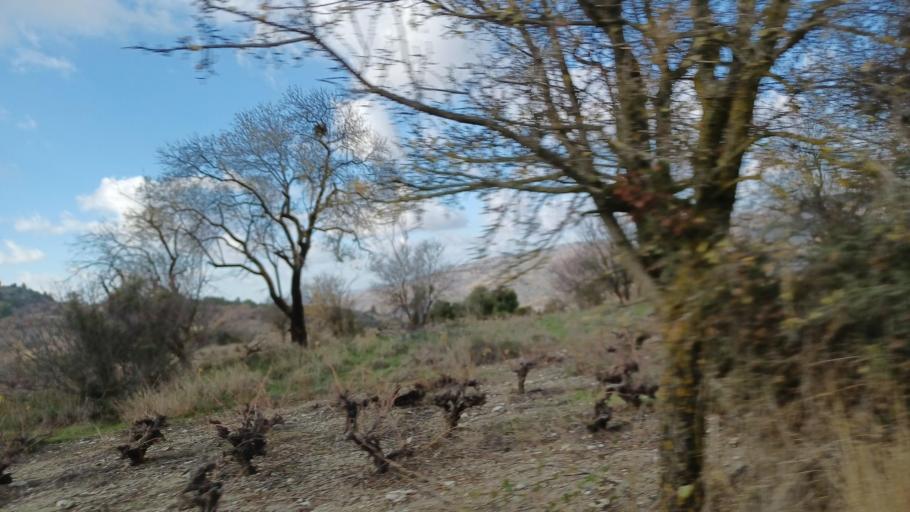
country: CY
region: Limassol
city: Pachna
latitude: 34.8587
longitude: 32.6915
